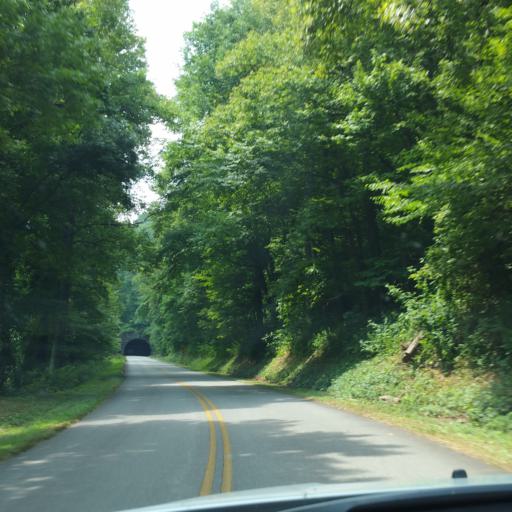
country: US
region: North Carolina
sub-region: Buncombe County
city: Bent Creek
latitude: 35.4724
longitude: -82.6224
